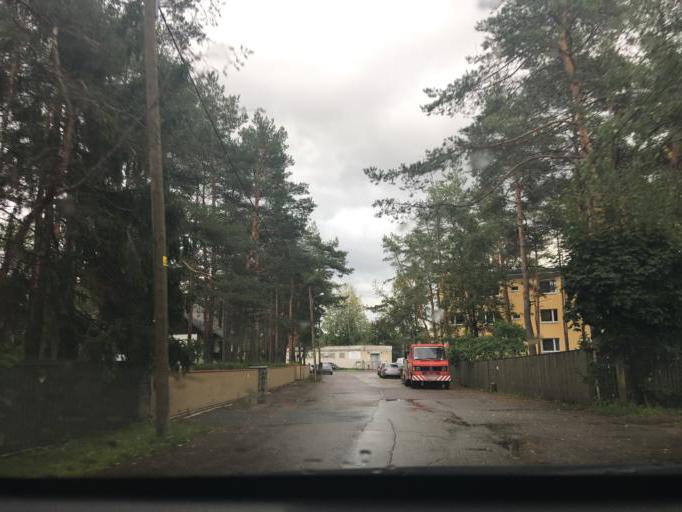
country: EE
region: Harju
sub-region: Saue vald
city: Laagri
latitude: 59.3715
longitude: 24.6748
